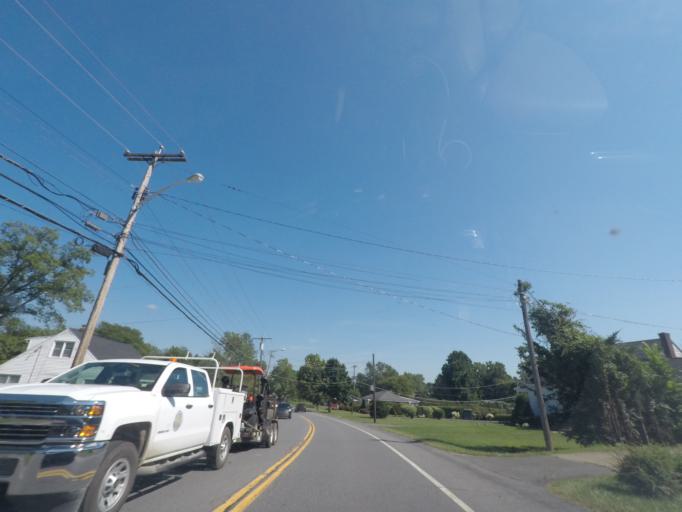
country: US
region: New York
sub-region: Albany County
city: Menands
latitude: 42.7345
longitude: -73.7560
